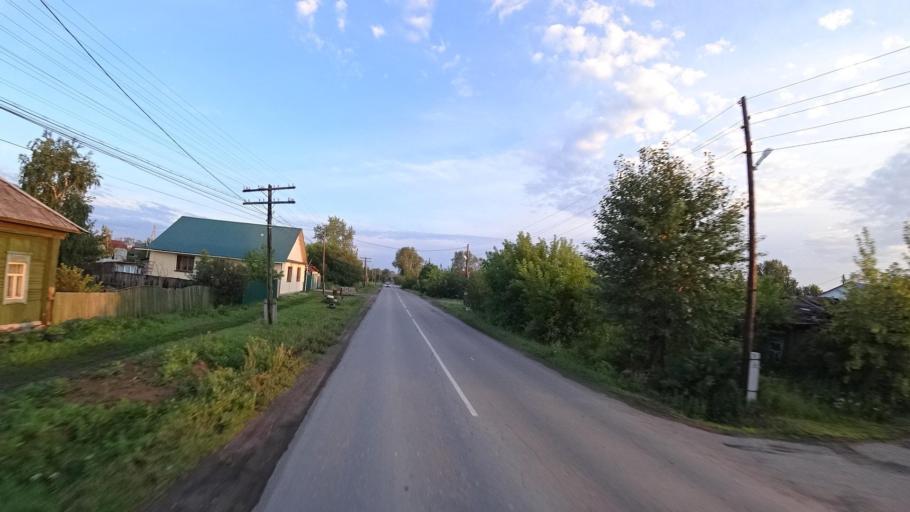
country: RU
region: Sverdlovsk
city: Kamyshlov
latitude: 56.8621
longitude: 62.7089
